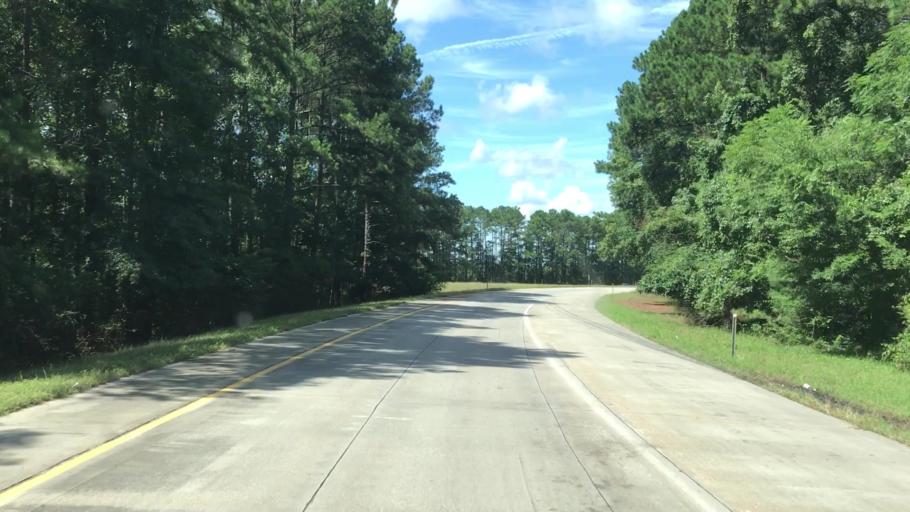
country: US
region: Georgia
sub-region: Taliaferro County
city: Crawfordville
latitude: 33.4996
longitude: -82.8074
